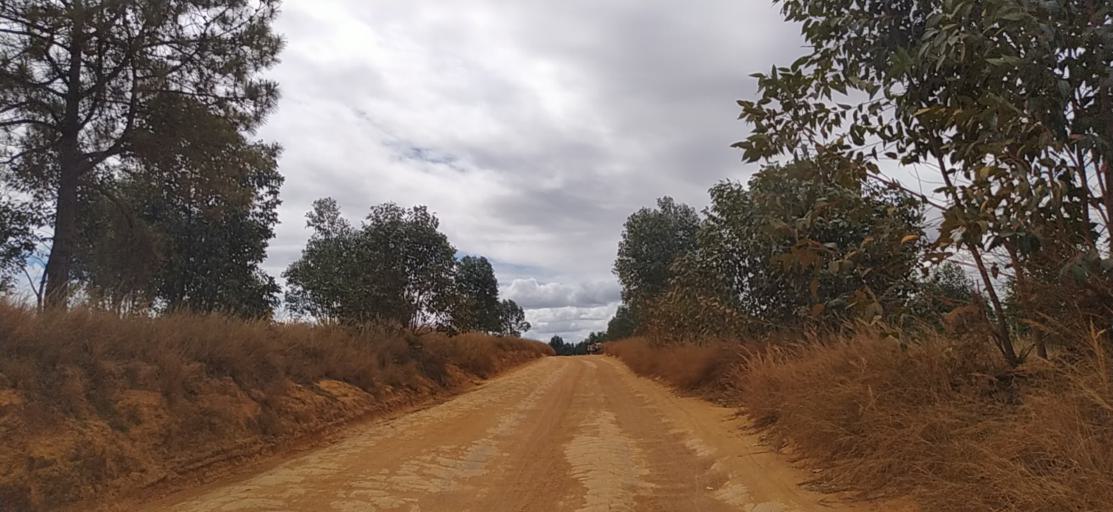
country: MG
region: Alaotra Mangoro
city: Ambatondrazaka
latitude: -17.9941
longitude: 48.2660
